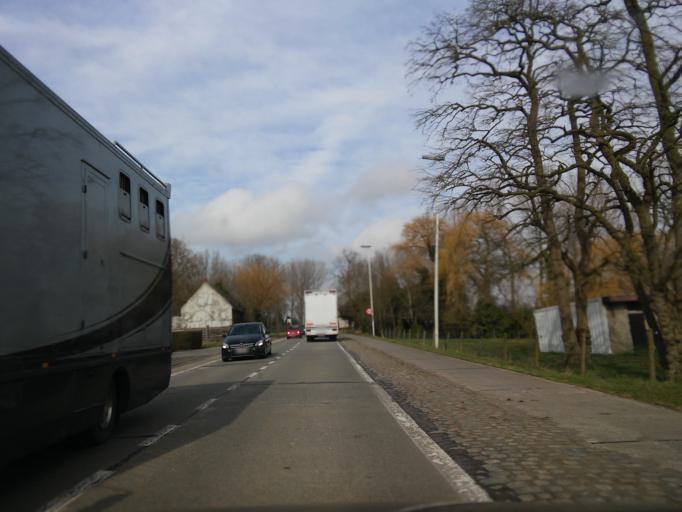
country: BE
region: Flanders
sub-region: Provincie Oost-Vlaanderen
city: Sint-Gillis-Waas
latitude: 51.2838
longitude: 4.1817
